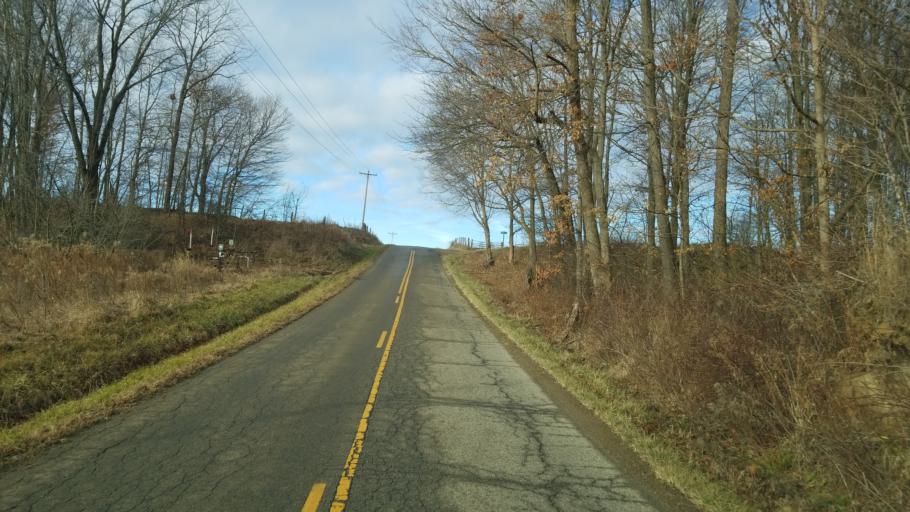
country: US
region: Ohio
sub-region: Knox County
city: Gambier
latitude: 40.3136
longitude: -82.3300
